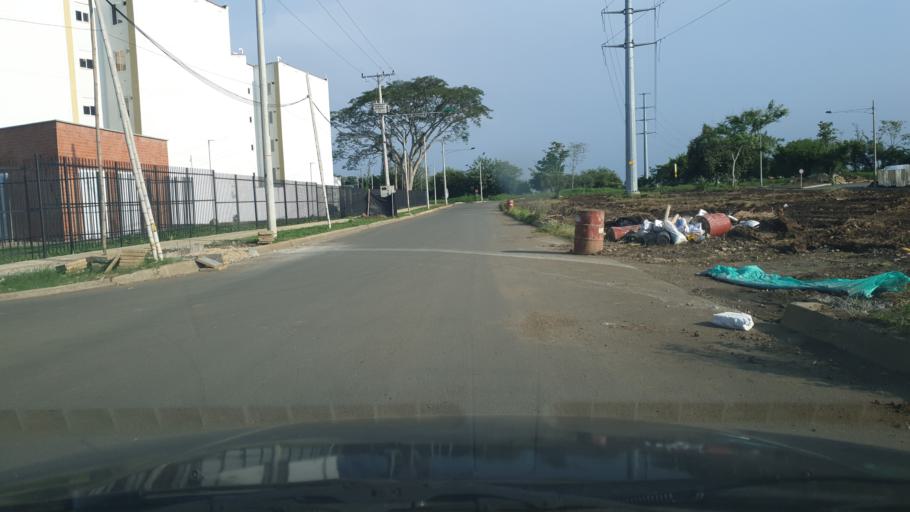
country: CO
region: Valle del Cauca
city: Jamundi
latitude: 3.3456
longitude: -76.5144
